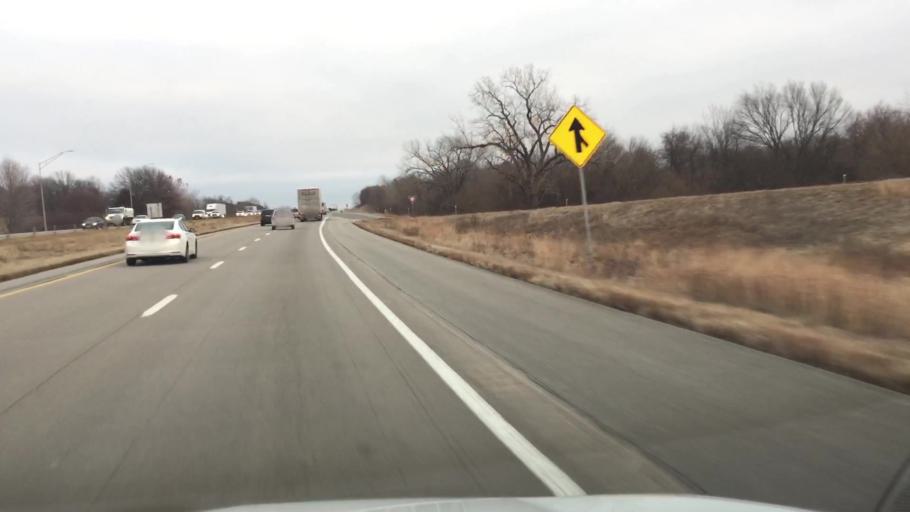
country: US
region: Iowa
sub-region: Jasper County
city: Newton
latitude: 41.6835
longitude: -93.0736
